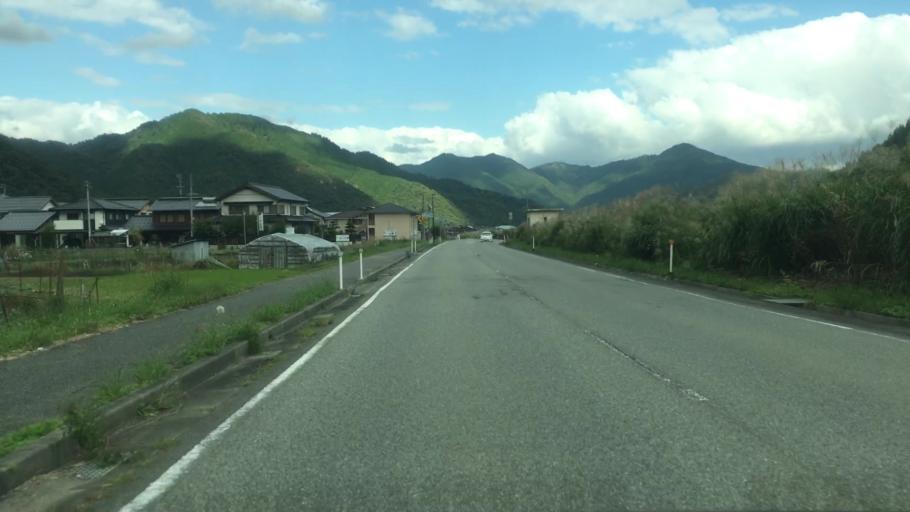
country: JP
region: Hyogo
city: Toyooka
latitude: 35.3728
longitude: 134.7659
